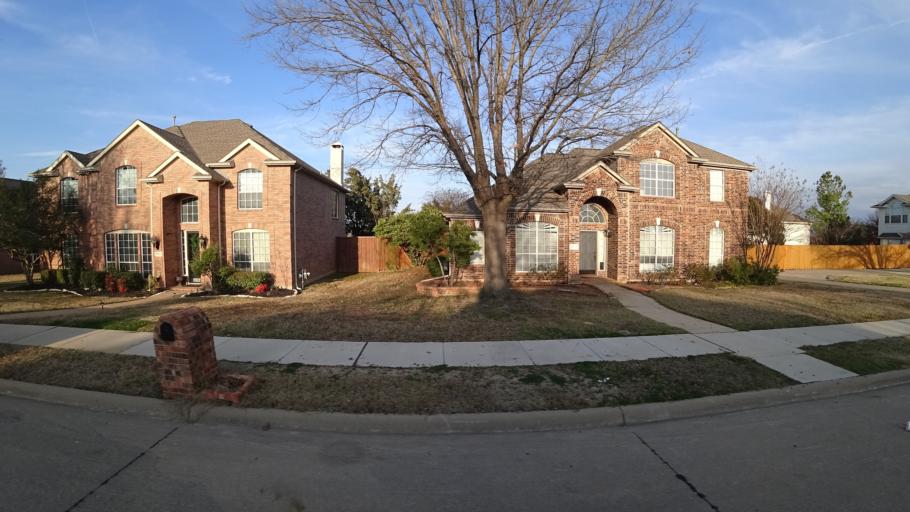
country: US
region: Texas
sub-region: Dallas County
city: Coppell
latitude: 32.9930
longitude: -96.9853
